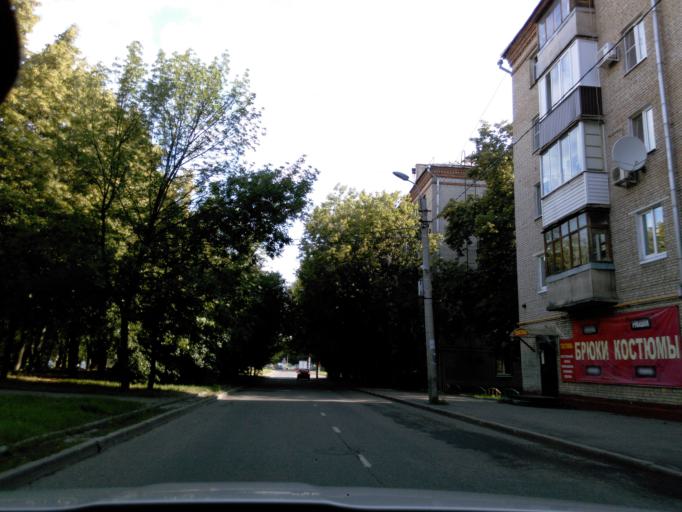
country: RU
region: Moskovskaya
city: Koptevo
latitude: 55.8297
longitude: 37.5260
